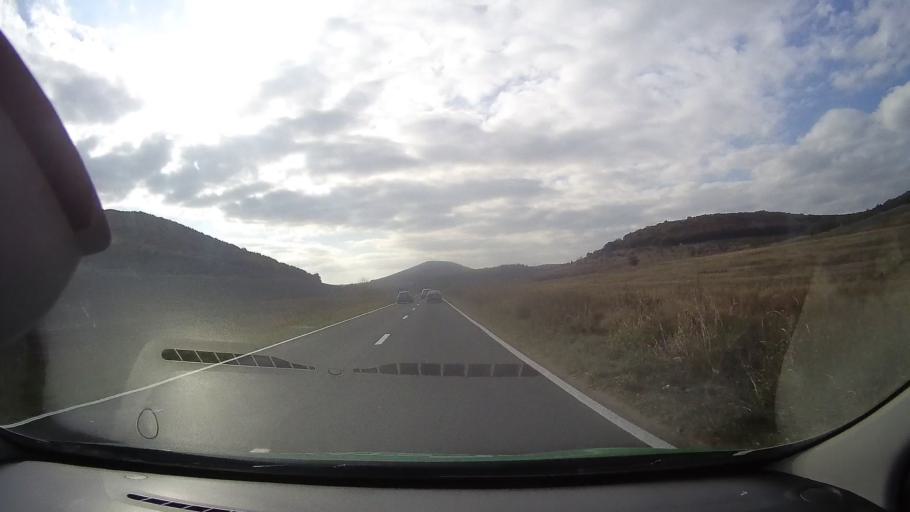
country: RO
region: Tulcea
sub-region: Comuna Ciucurova
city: Ciucurova
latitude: 44.9654
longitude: 28.5289
